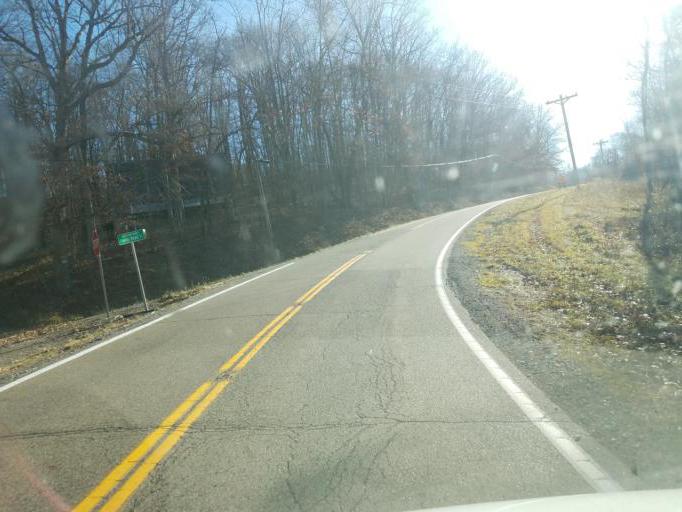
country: US
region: Ohio
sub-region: Muskingum County
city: Frazeysburg
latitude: 40.2625
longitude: -82.0840
